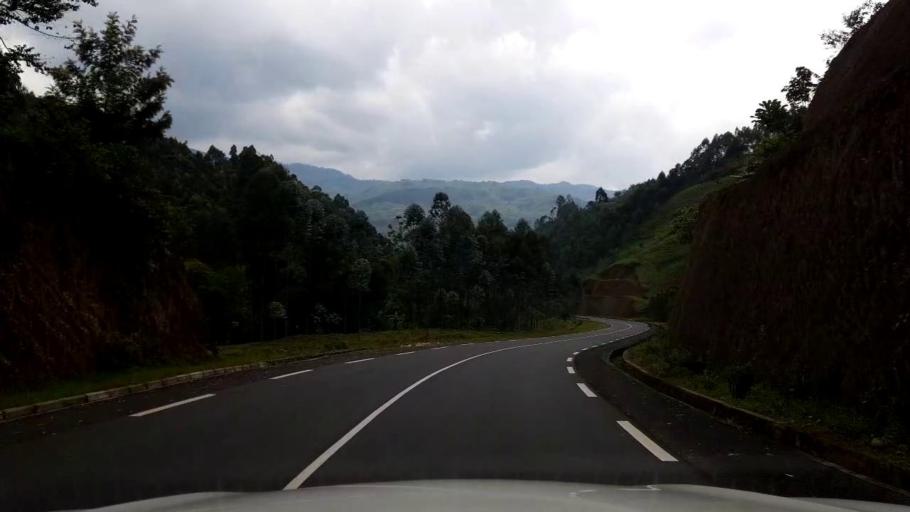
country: RW
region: Western Province
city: Kibuye
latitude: -1.9073
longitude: 29.3617
